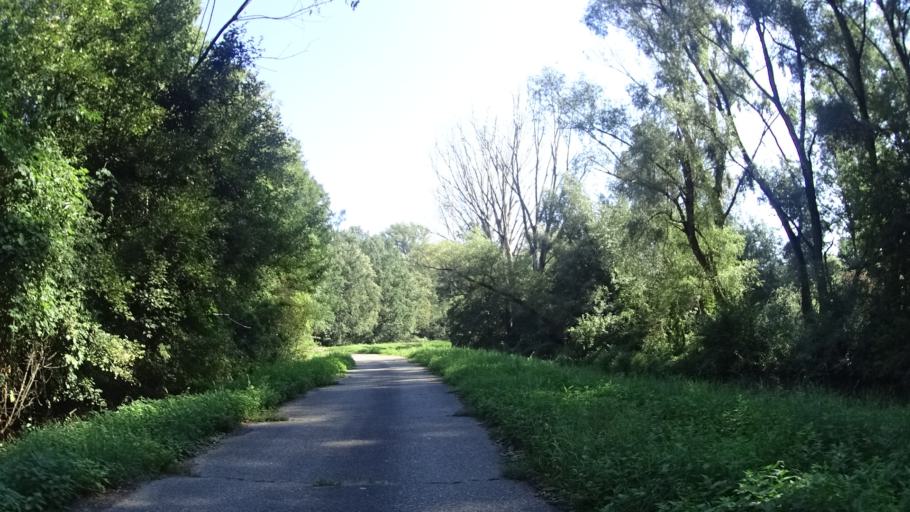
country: CZ
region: South Moravian
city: Hodonin
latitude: 48.8173
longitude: 17.1287
